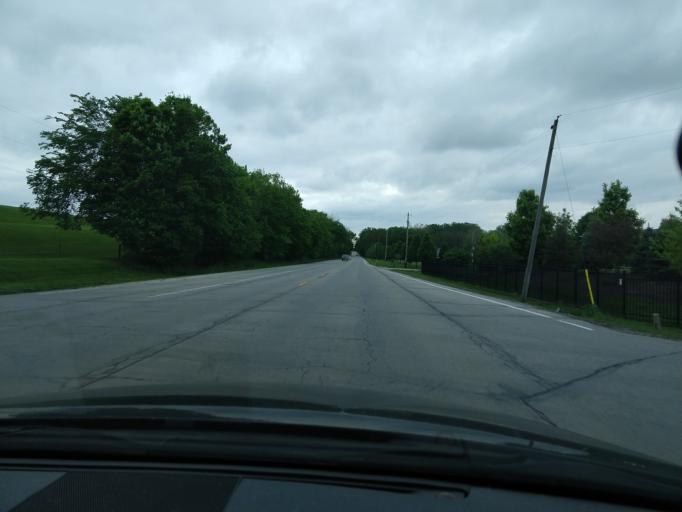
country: US
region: Indiana
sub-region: Hamilton County
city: Noblesville
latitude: 40.0522
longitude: -85.9292
